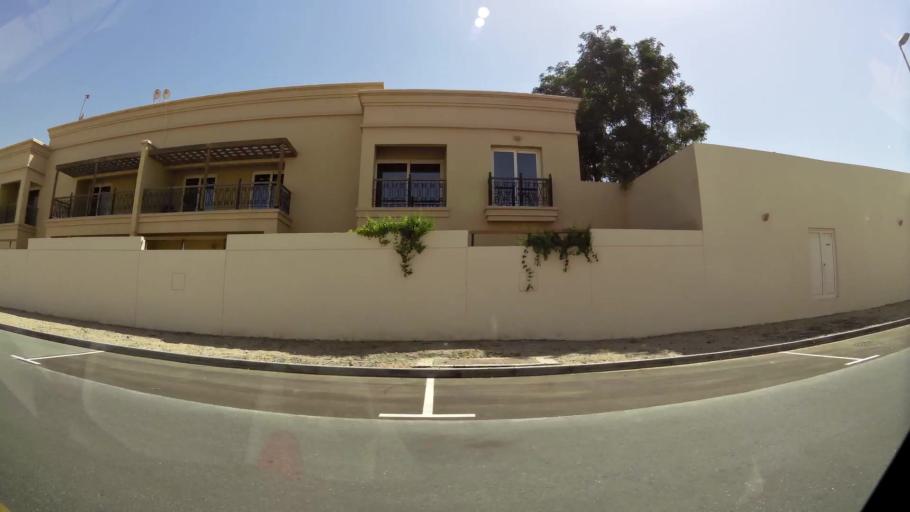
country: AE
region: Dubai
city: Dubai
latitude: 25.1083
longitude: 55.2008
